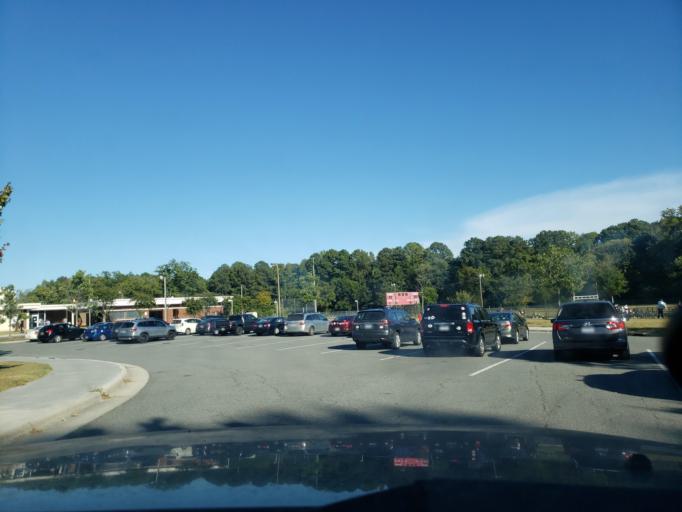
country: US
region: North Carolina
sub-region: Durham County
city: Durham
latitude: 35.9647
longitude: -78.9011
